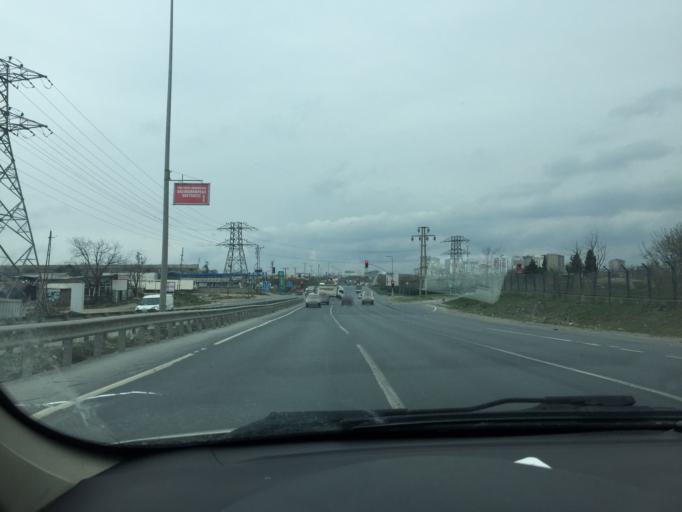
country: TR
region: Istanbul
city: Basaksehir
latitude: 41.1363
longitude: 28.8144
